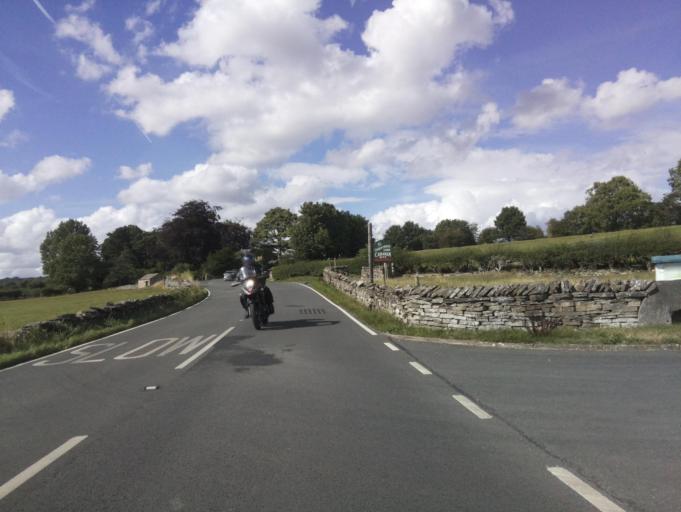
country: GB
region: England
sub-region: North Yorkshire
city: Leyburn
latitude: 54.3030
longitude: -1.8236
